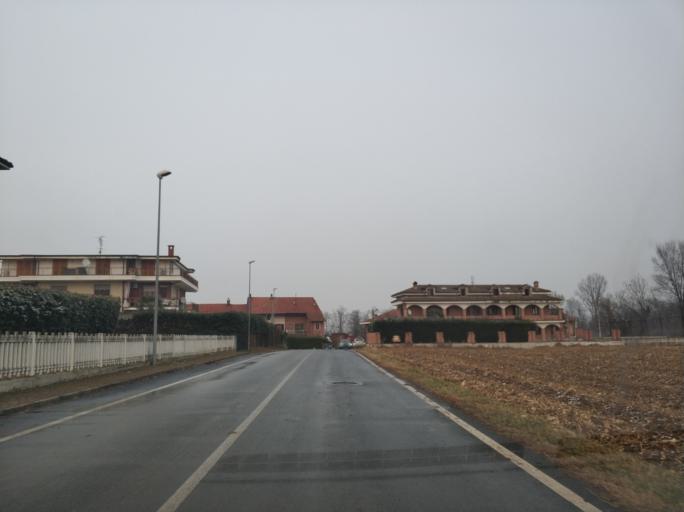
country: IT
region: Piedmont
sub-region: Provincia di Torino
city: San Francesco al Campo
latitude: 45.2260
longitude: 7.6628
